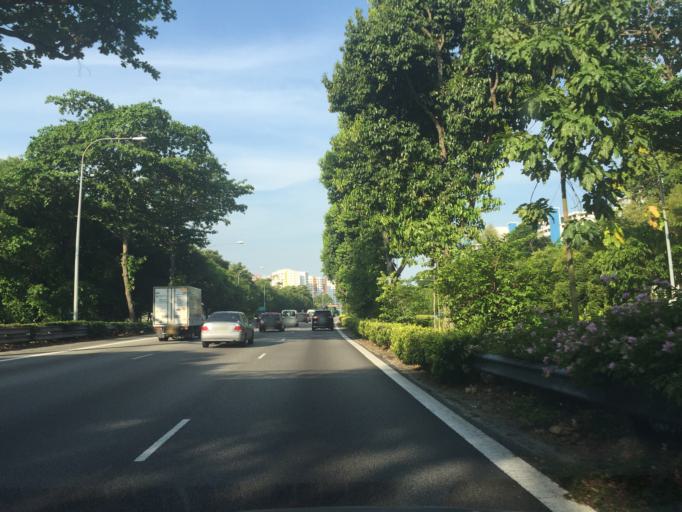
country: SG
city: Singapore
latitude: 1.3355
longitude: 103.9279
